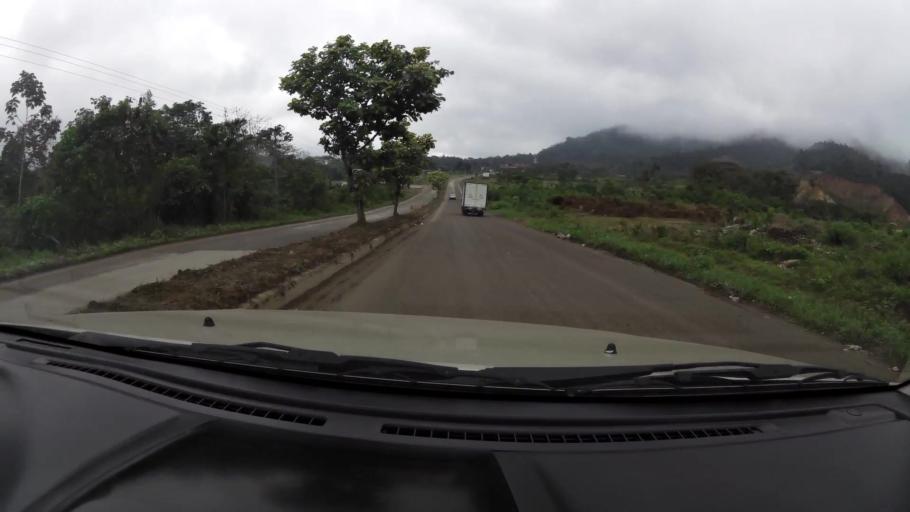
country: EC
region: El Oro
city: Pasaje
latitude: -3.3285
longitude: -79.7752
